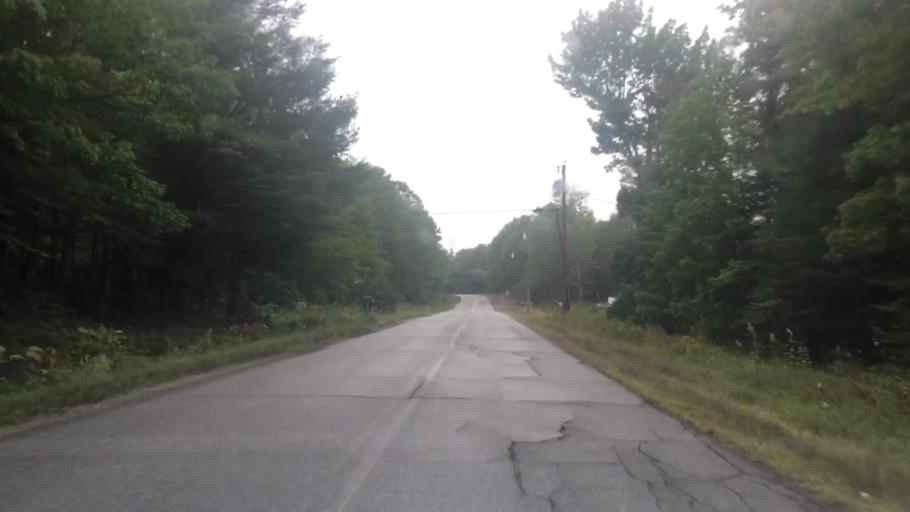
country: US
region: Maine
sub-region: Waldo County
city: Stockton Springs
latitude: 44.5408
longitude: -68.9079
